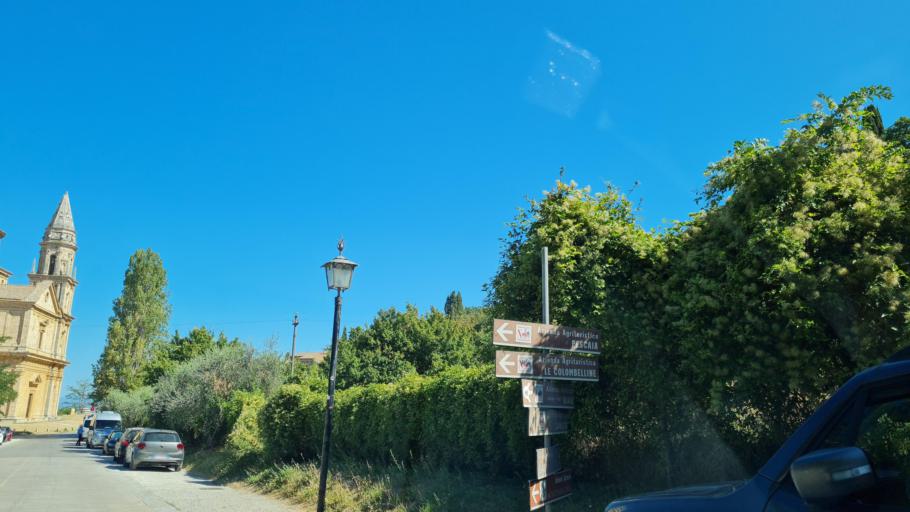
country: IT
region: Tuscany
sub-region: Provincia di Siena
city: Montepulciano
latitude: 43.0894
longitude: 11.7753
